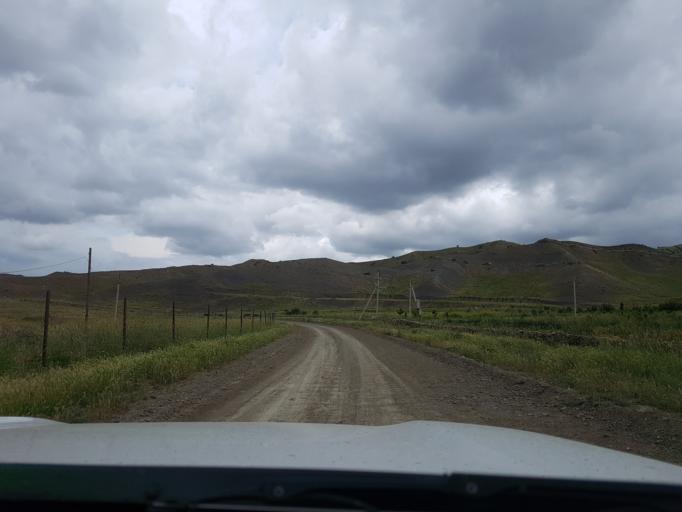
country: TM
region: Ahal
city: Baharly
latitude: 38.2156
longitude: 56.9939
